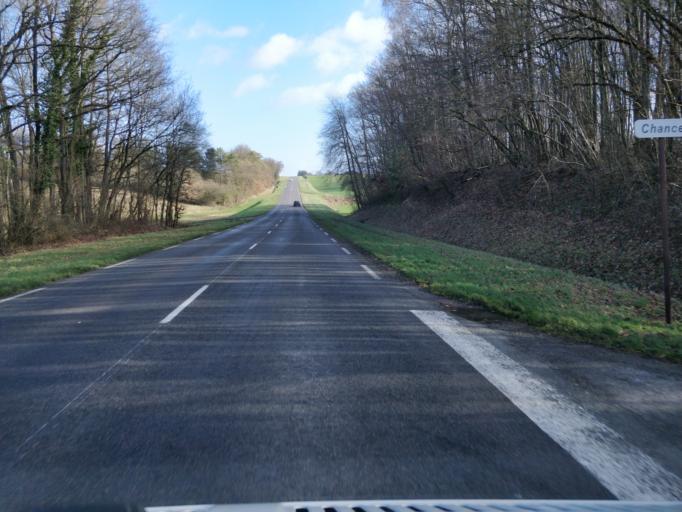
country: FR
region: Ile-de-France
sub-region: Departement de Seine-et-Marne
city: Lorrez-le-Bocage-Preaux
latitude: 48.2205
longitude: 2.8646
